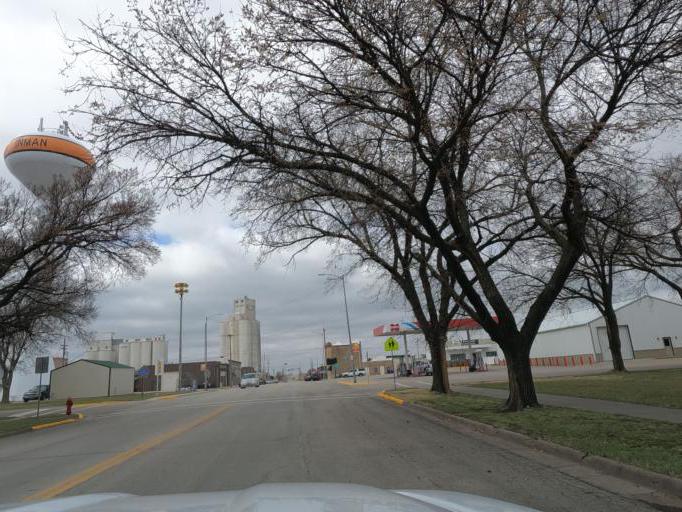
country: US
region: Kansas
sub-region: McPherson County
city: Inman
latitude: 38.2320
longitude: -97.7743
